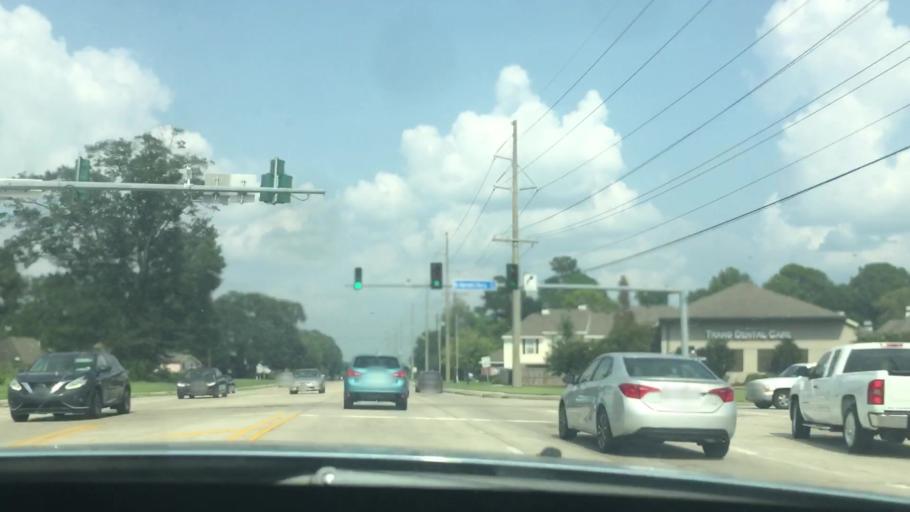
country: US
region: Louisiana
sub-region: East Baton Rouge Parish
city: Westminster
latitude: 30.4344
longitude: -91.0666
